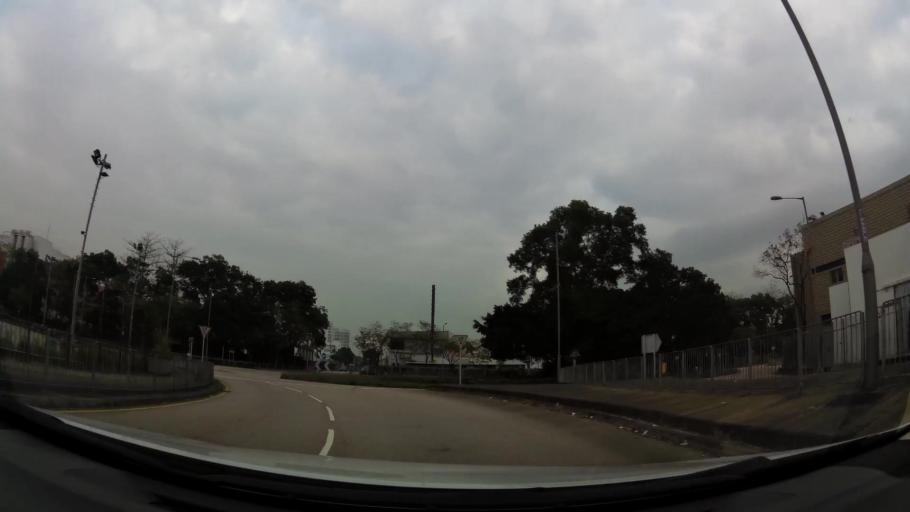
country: HK
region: Tai Po
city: Tai Po
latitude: 22.4570
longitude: 114.1793
